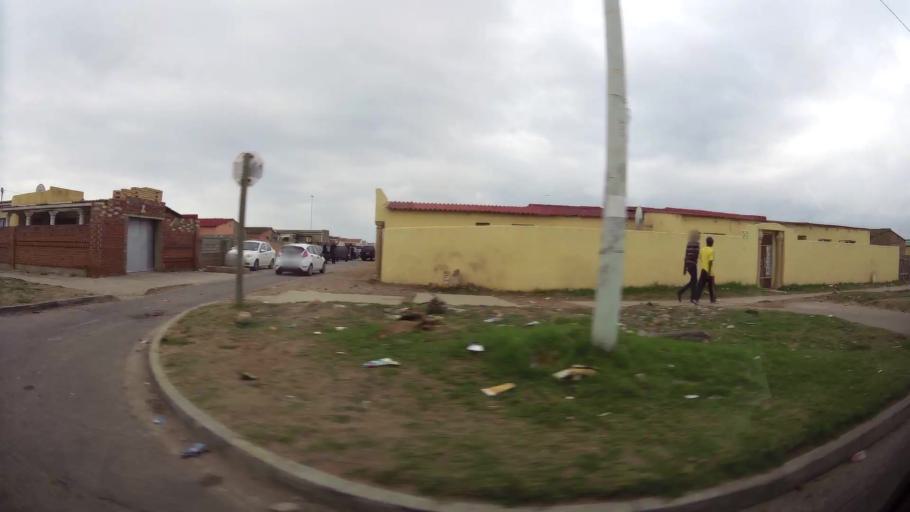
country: ZA
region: Eastern Cape
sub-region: Nelson Mandela Bay Metropolitan Municipality
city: Port Elizabeth
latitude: -33.8966
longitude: 25.6006
